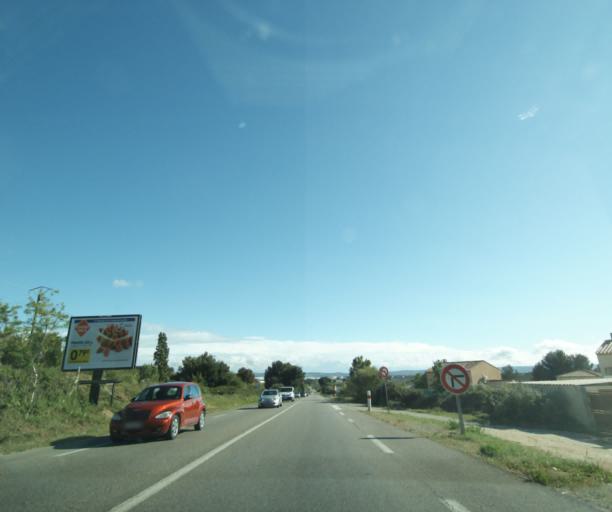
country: FR
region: Provence-Alpes-Cote d'Azur
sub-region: Departement des Bouches-du-Rhone
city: Vitrolles
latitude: 43.4565
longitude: 5.2325
